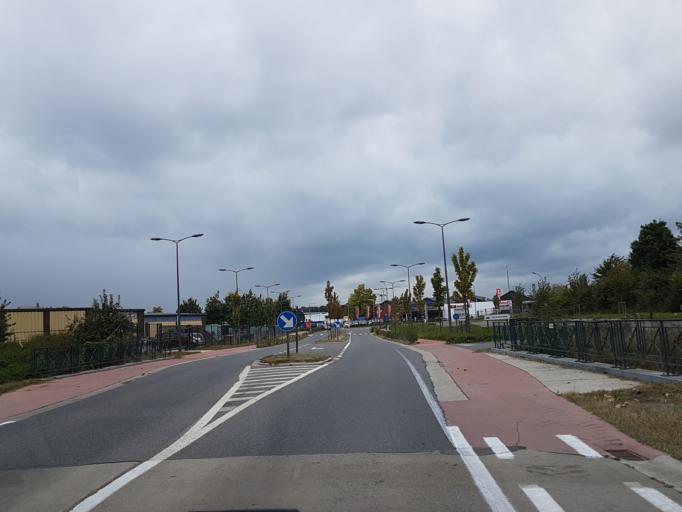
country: BE
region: Flanders
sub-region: Provincie Vlaams-Brabant
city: Tienen
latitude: 50.8055
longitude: 4.9622
